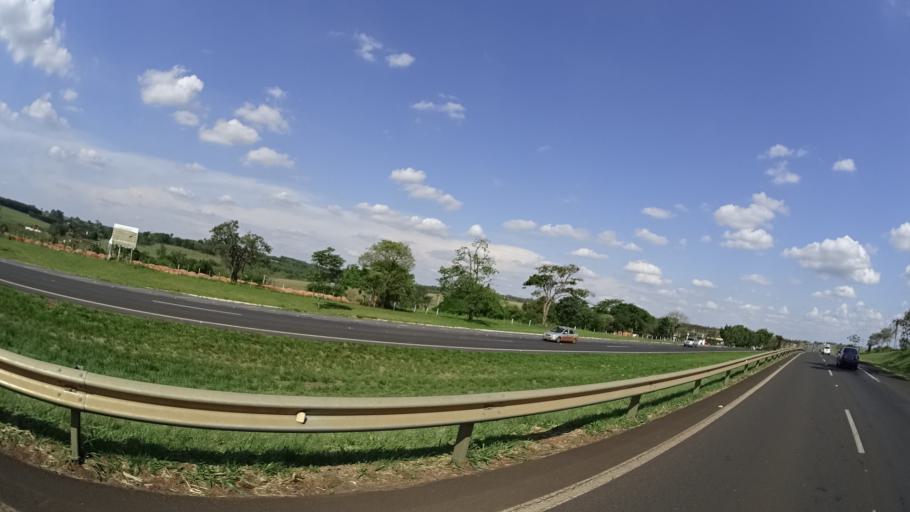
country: BR
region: Sao Paulo
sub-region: Sao Jose Do Rio Preto
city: Sao Jose do Rio Preto
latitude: -20.8953
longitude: -49.3044
